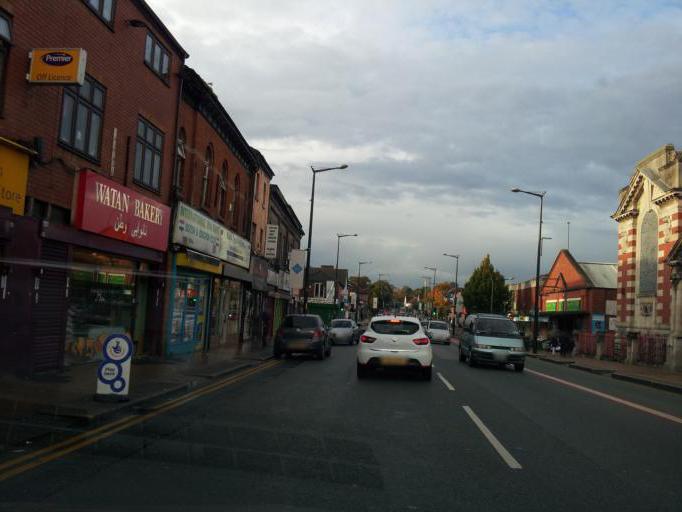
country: GB
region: England
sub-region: Manchester
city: Crumpsall
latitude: 53.5113
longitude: -2.2446
